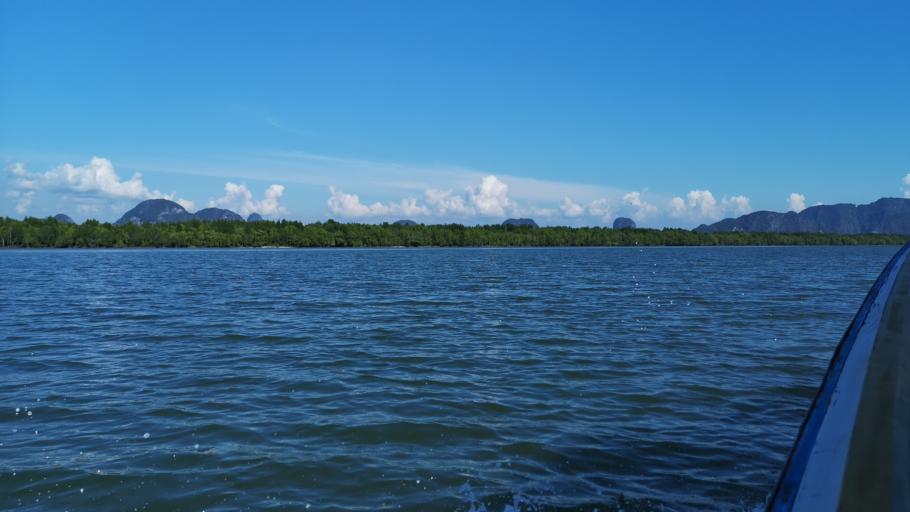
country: TH
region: Phangnga
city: Takua Thung
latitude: 8.3101
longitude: 98.4398
